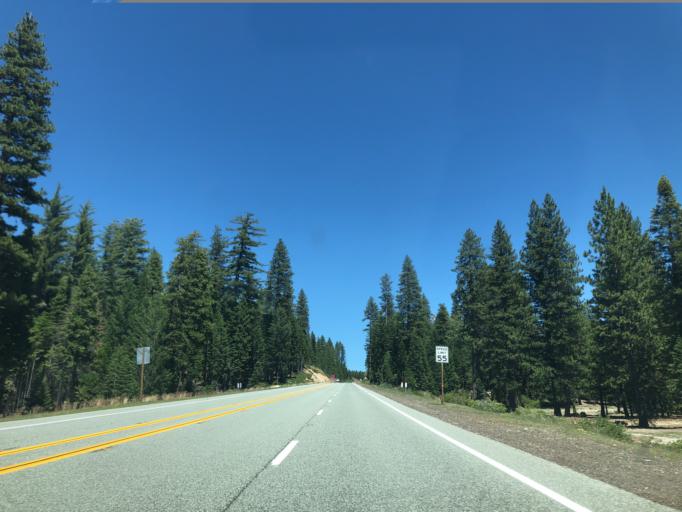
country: US
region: California
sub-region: Shasta County
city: Shingletown
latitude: 40.5355
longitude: -121.6160
